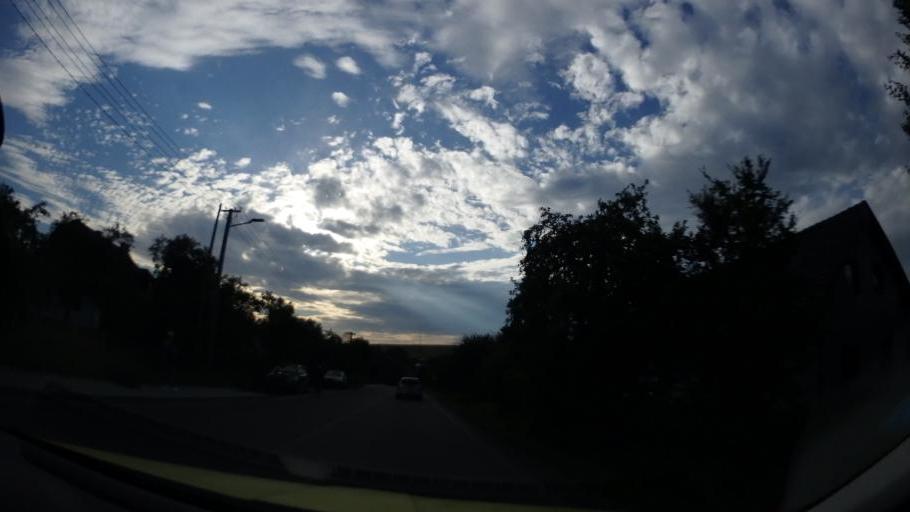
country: CZ
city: Rybi
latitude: 49.5992
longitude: 18.0836
